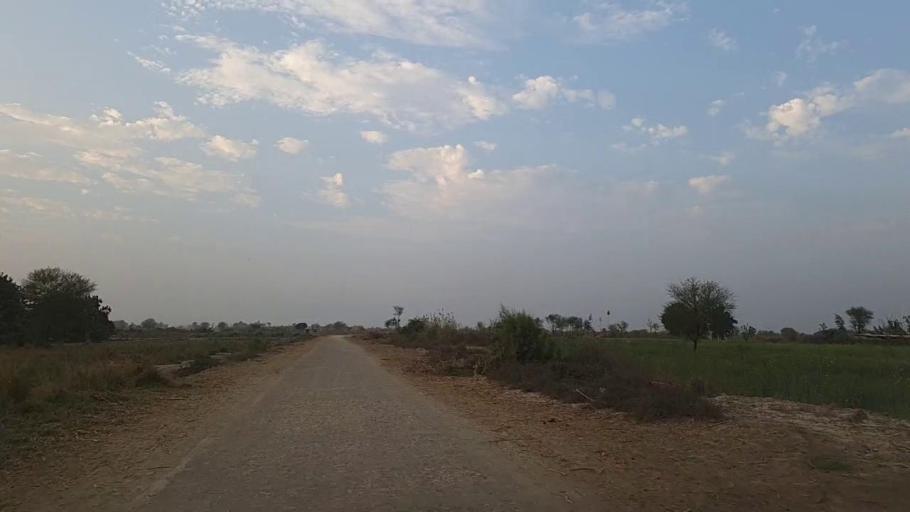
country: PK
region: Sindh
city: Mirwah Gorchani
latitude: 25.3464
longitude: 69.2036
